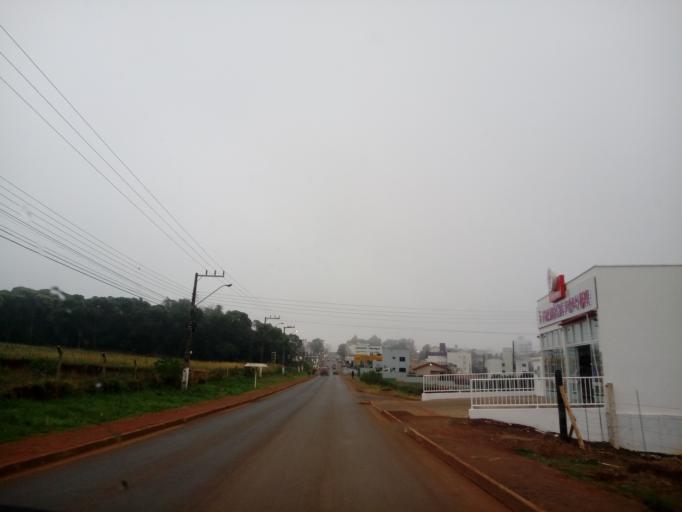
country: BR
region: Santa Catarina
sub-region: Chapeco
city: Chapeco
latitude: -27.1047
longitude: -52.6735
